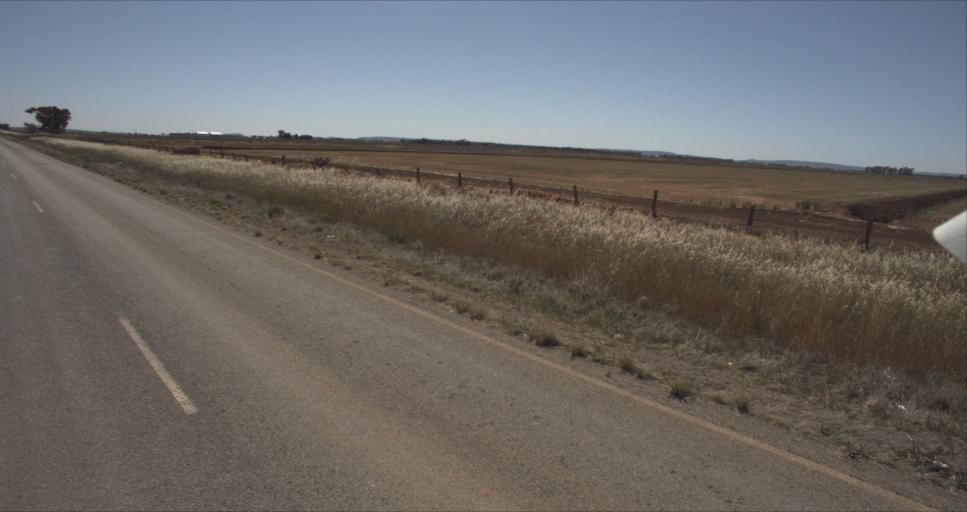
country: AU
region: New South Wales
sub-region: Leeton
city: Leeton
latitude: -34.5157
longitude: 146.2842
